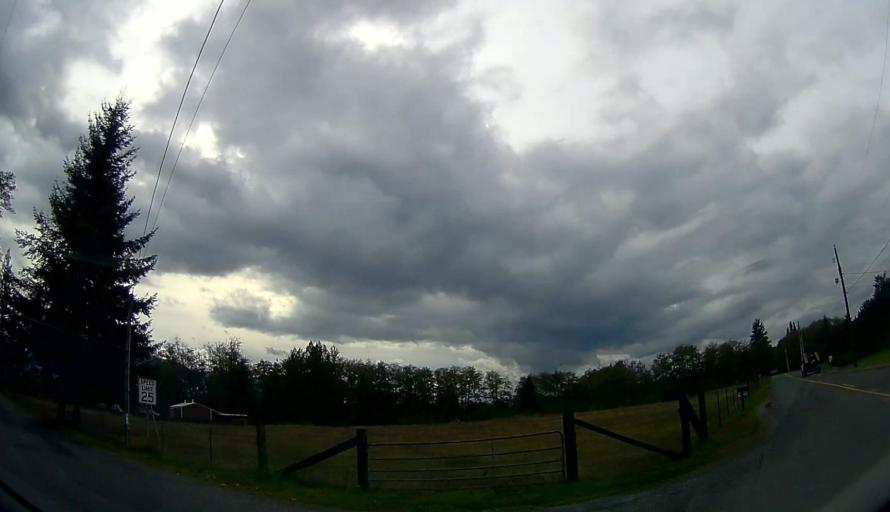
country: US
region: Washington
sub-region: Skagit County
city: Sedro-Woolley
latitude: 48.5339
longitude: -122.0279
